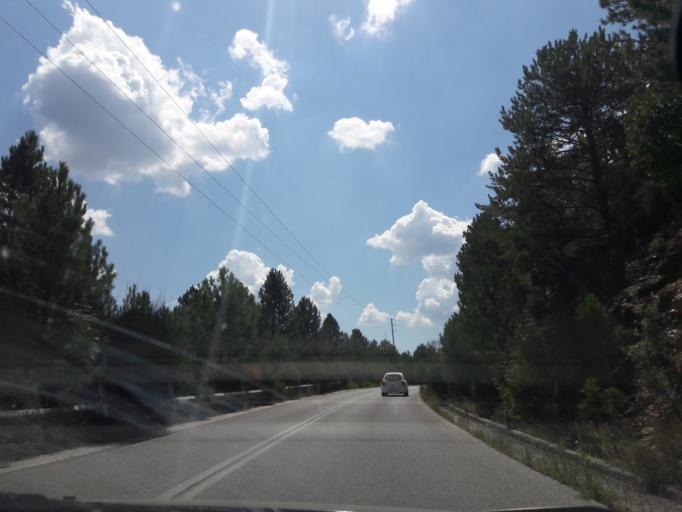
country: GR
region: Central Macedonia
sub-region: Nomos Chalkidikis
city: Polygyros
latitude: 40.3652
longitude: 23.4981
